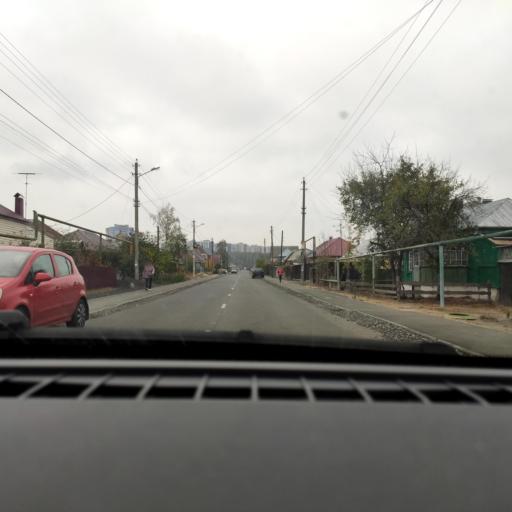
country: RU
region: Voronezj
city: Somovo
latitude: 51.7469
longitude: 39.3290
